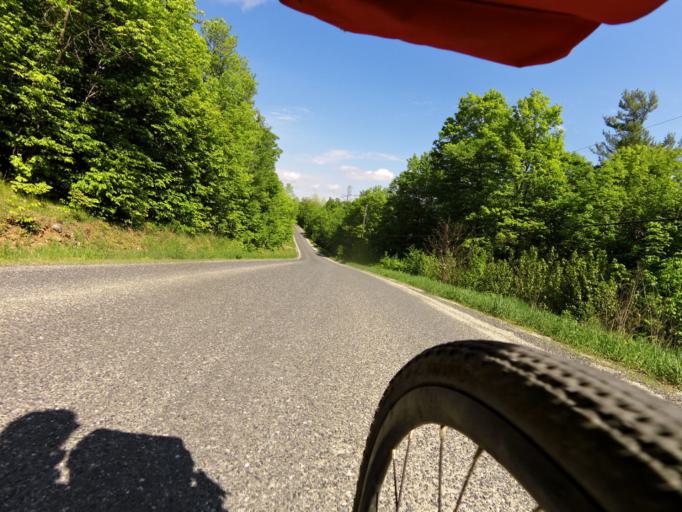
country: CA
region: Ontario
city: Renfrew
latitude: 45.1395
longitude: -76.6134
